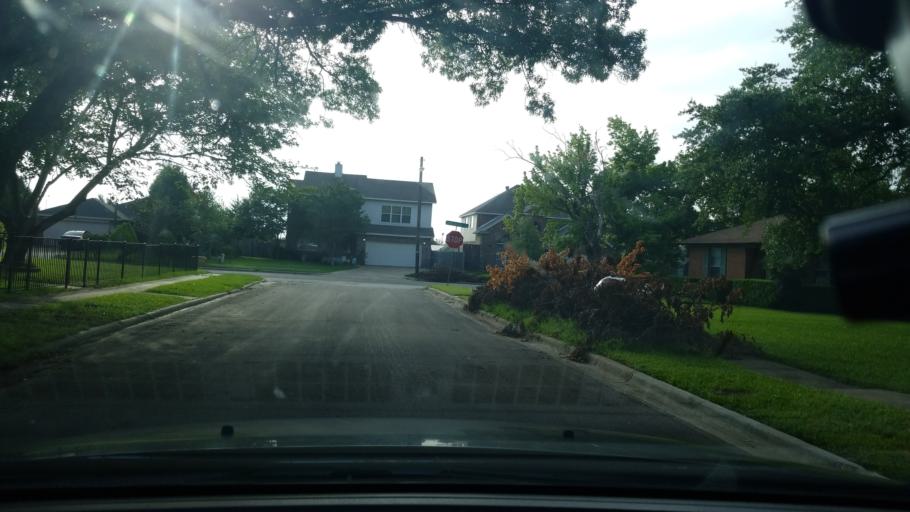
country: US
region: Texas
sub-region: Dallas County
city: Garland
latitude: 32.8313
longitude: -96.6612
